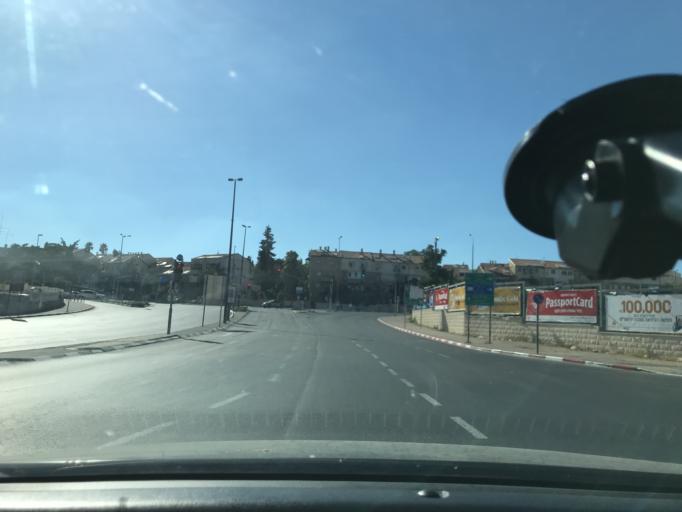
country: IL
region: Jerusalem
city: West Jerusalem
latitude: 31.7851
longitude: 35.1991
